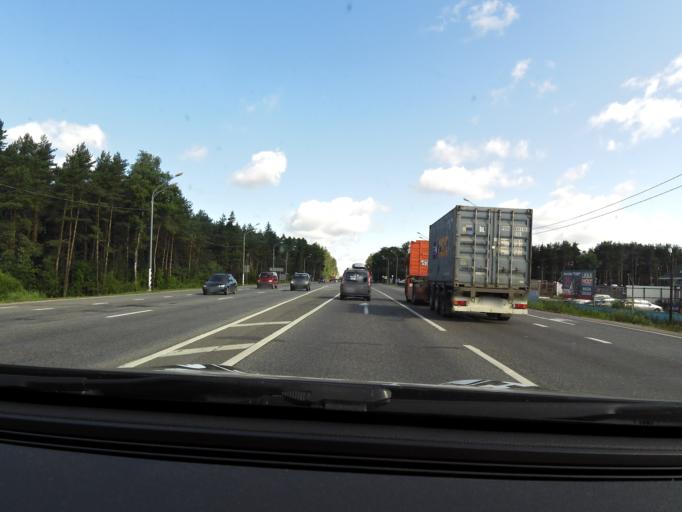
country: RU
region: Tverskaya
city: Tver
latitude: 56.8690
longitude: 35.7865
